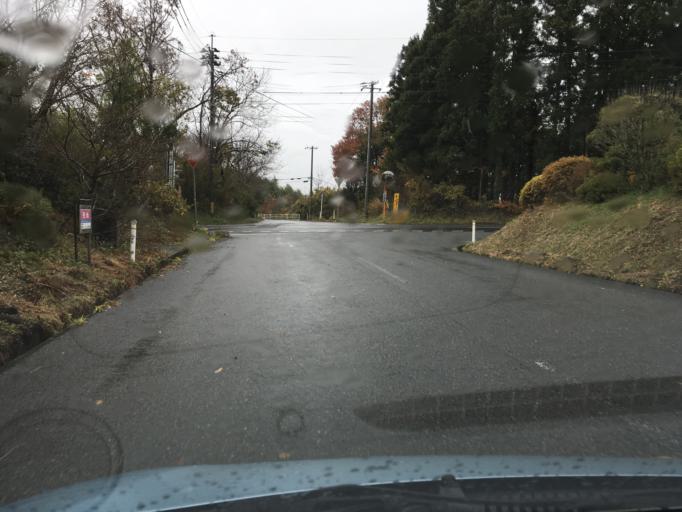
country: JP
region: Iwate
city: Ichinoseki
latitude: 38.7881
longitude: 141.2319
